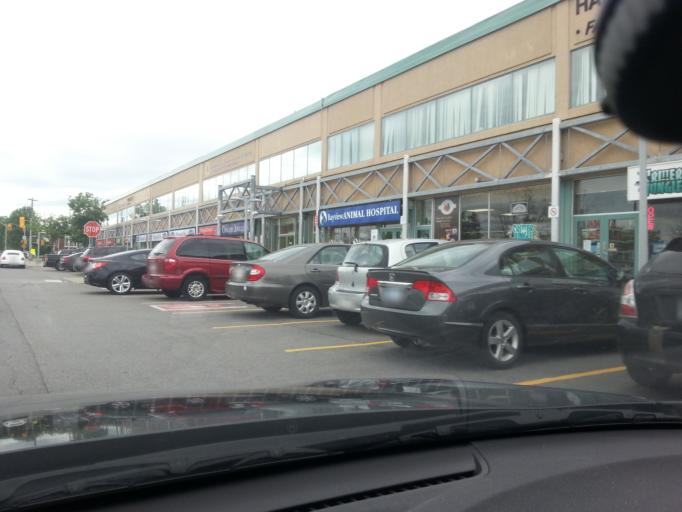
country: CA
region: Ontario
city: Ottawa
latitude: 45.3861
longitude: -75.7397
